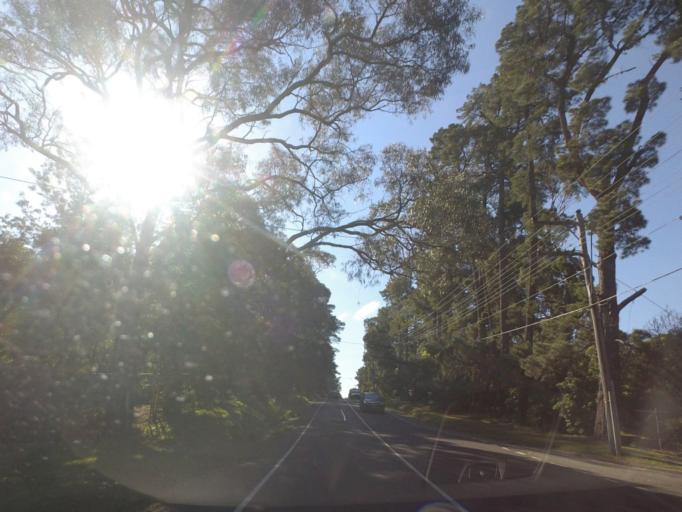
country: AU
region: Victoria
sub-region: Manningham
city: Donvale
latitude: -37.7907
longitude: 145.1802
